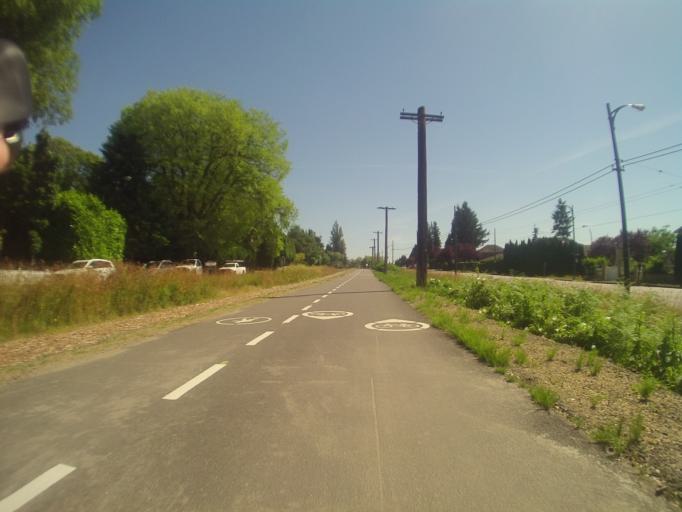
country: CA
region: British Columbia
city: Vancouver
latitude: 49.2541
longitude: -123.1529
